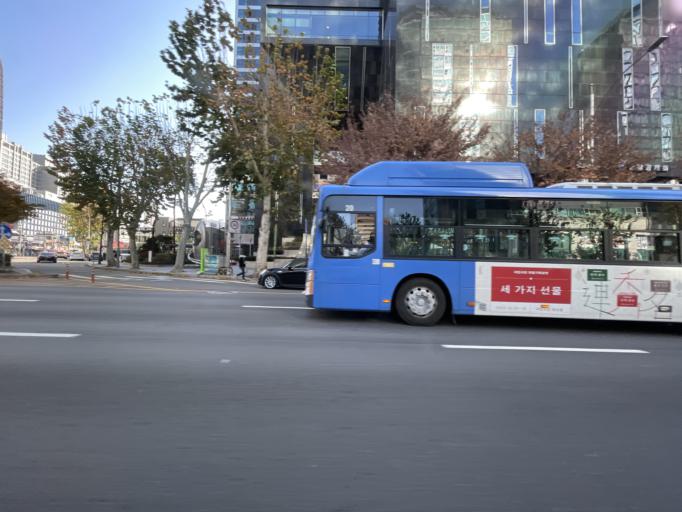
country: KR
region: Seoul
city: Seoul
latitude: 37.5422
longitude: 126.9497
